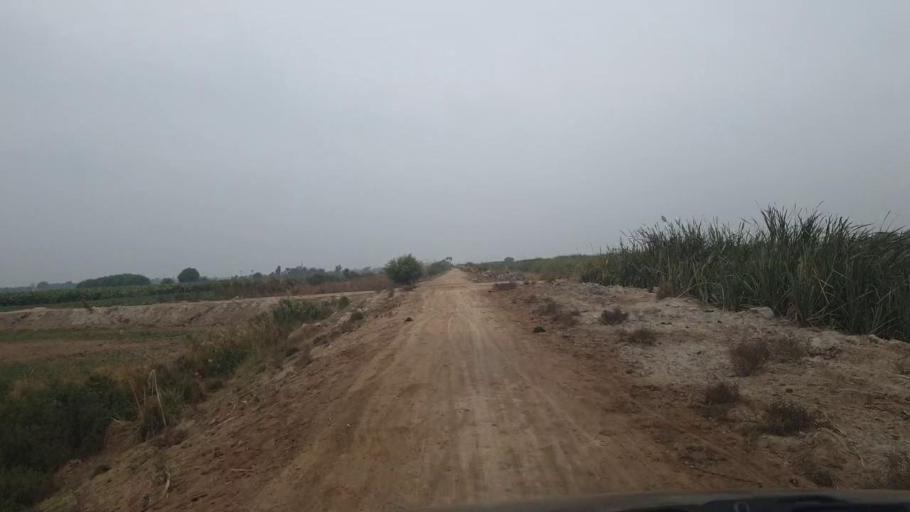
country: PK
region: Sindh
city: Shahdadpur
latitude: 25.8606
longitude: 68.7054
